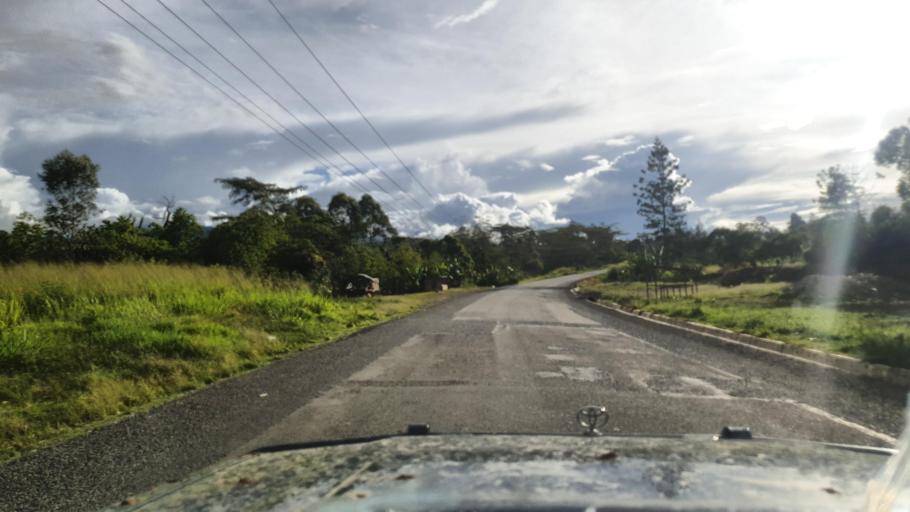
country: PG
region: Jiwaka
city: Minj
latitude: -5.8780
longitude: 144.7045
